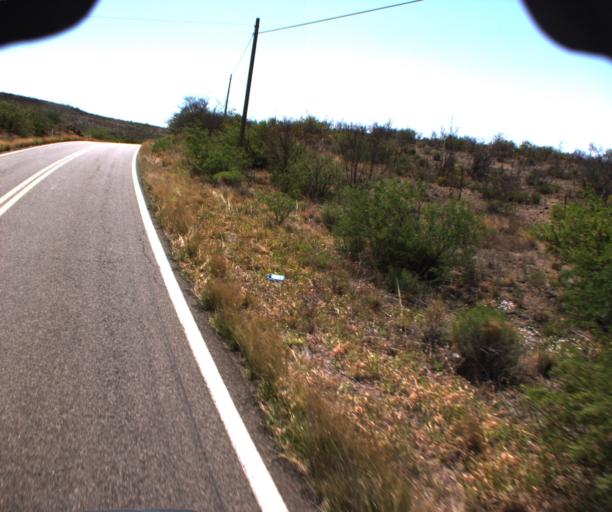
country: US
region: Arizona
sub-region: Cochise County
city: Douglas
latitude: 31.4731
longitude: -109.3909
